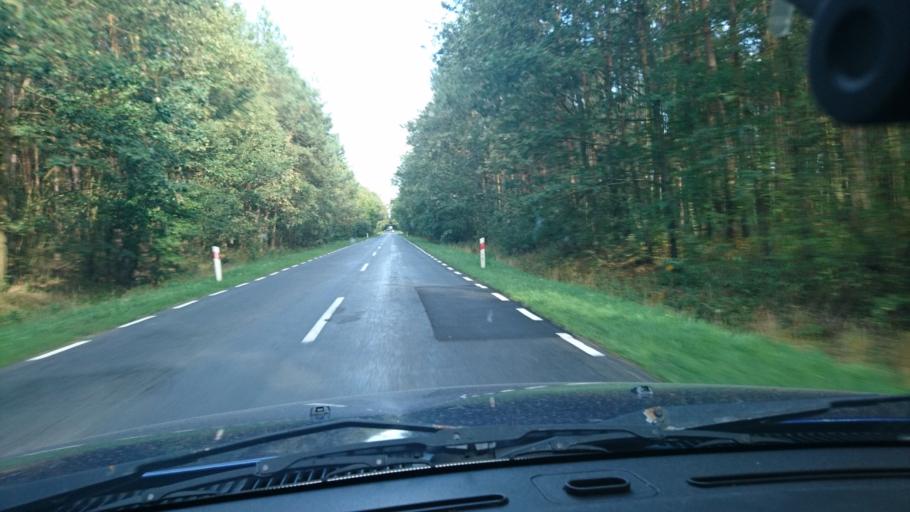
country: PL
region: Greater Poland Voivodeship
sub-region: Powiat krotoszynski
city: Sulmierzyce
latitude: 51.6003
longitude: 17.5953
